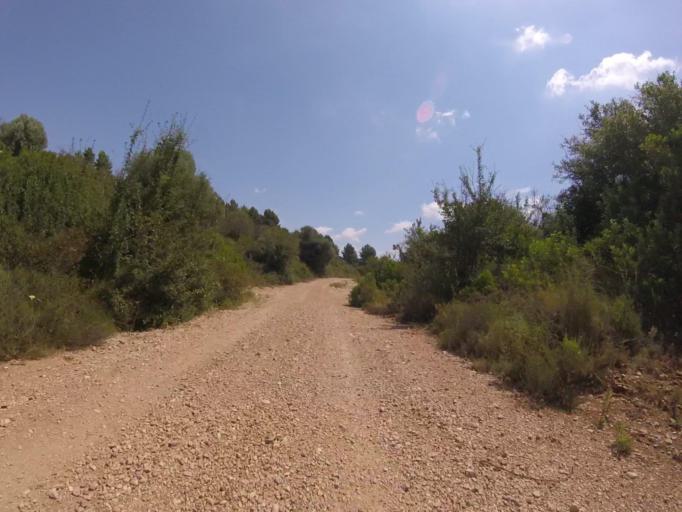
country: ES
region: Valencia
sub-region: Provincia de Castello
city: Torreblanca
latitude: 40.2131
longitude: 0.1419
